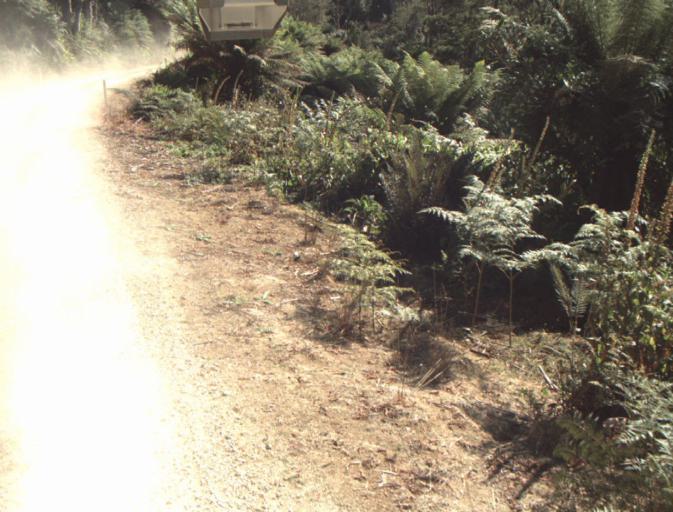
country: AU
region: Tasmania
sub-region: Dorset
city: Scottsdale
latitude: -41.2742
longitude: 147.3630
